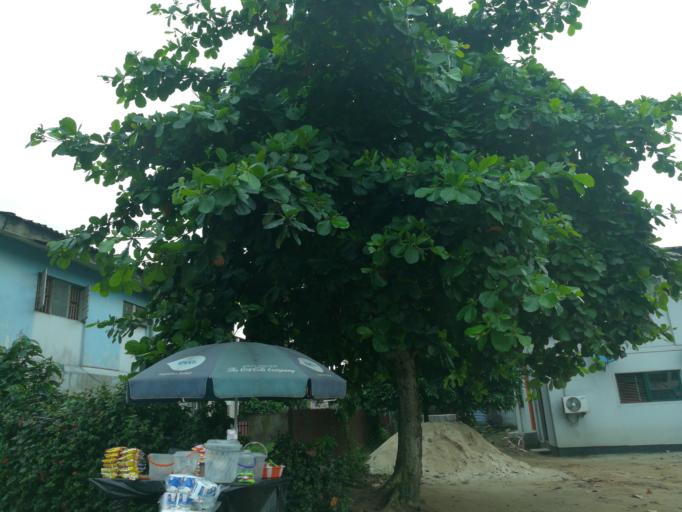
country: NG
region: Rivers
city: Port Harcourt
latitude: 4.8209
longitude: 7.0258
